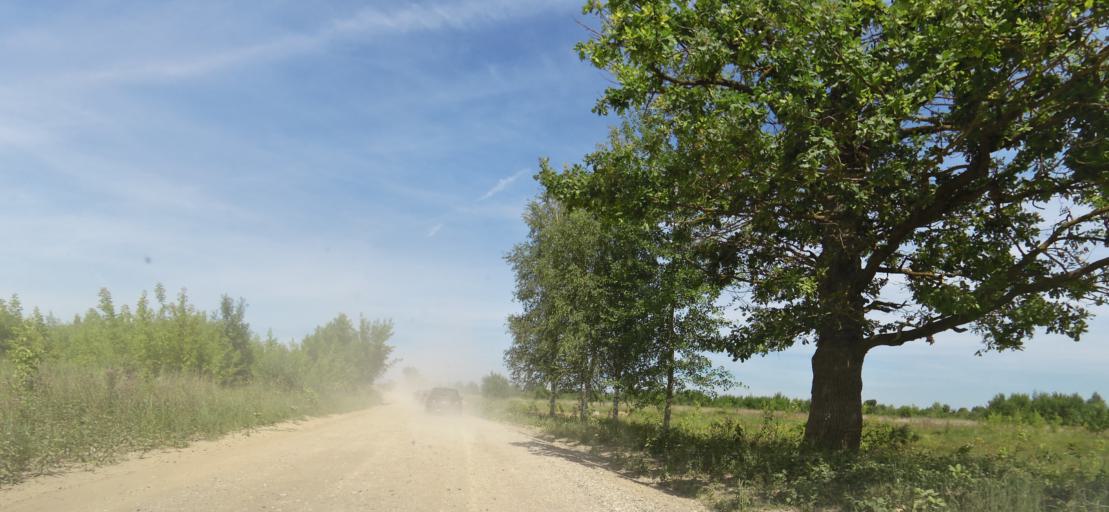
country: LT
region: Panevezys
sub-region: Panevezys City
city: Panevezys
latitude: 55.7238
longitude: 24.2965
